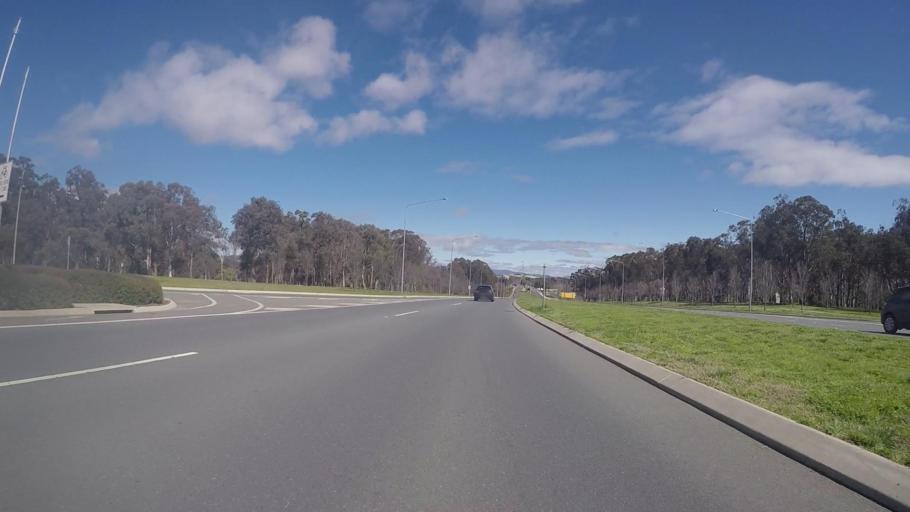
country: AU
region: Australian Capital Territory
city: Forrest
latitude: -35.2992
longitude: 149.1476
